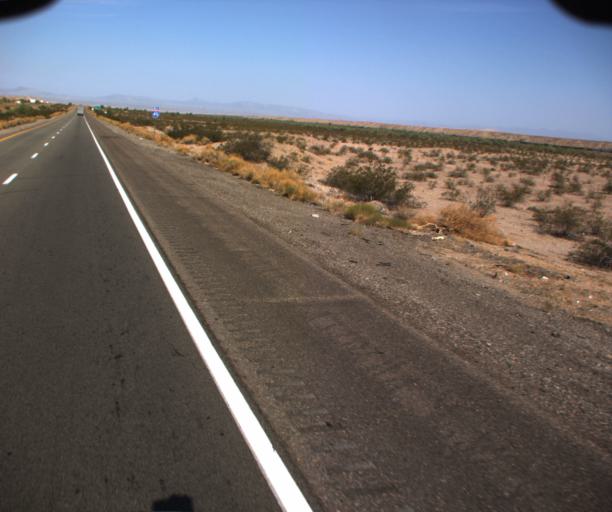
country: US
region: Arizona
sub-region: Mohave County
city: Desert Hills
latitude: 34.7295
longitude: -114.3256
